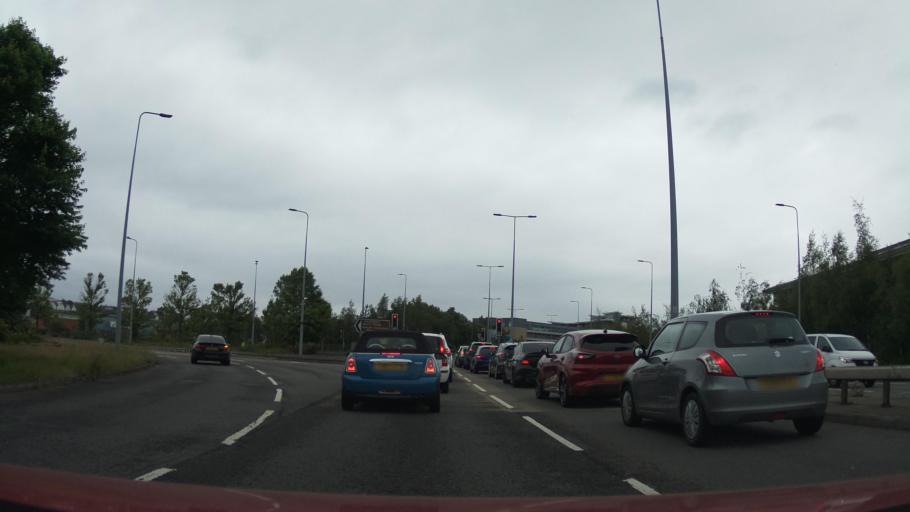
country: GB
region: Wales
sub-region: Vale of Glamorgan
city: Penarth
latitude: 51.4521
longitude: -3.1845
